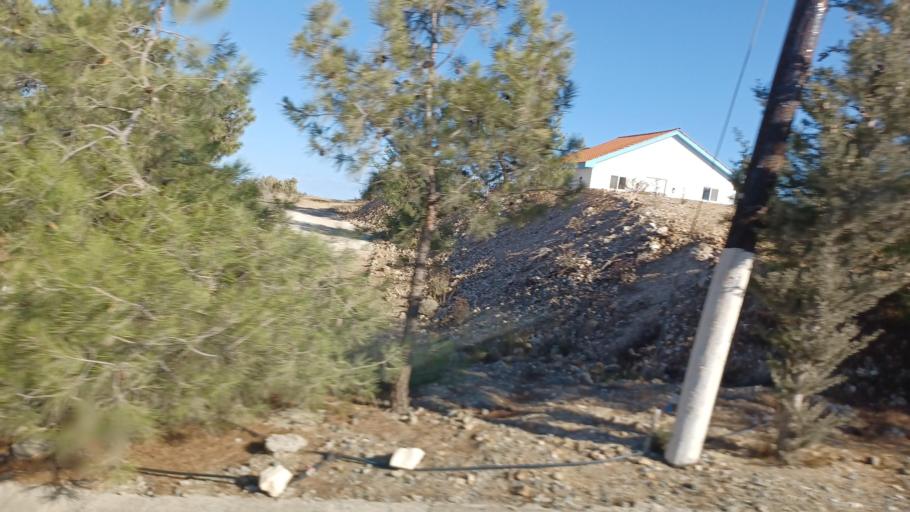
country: CY
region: Limassol
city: Pyrgos
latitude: 34.7731
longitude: 33.2473
